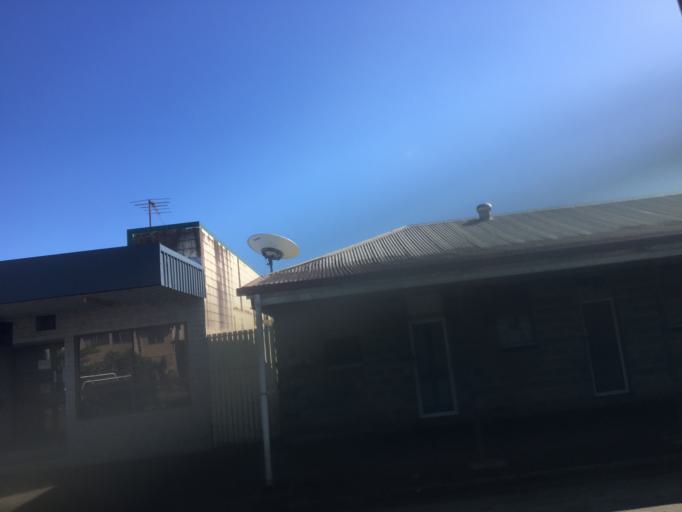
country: AU
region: Queensland
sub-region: Cassowary Coast
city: Innisfail
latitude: -17.5261
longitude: 146.0292
